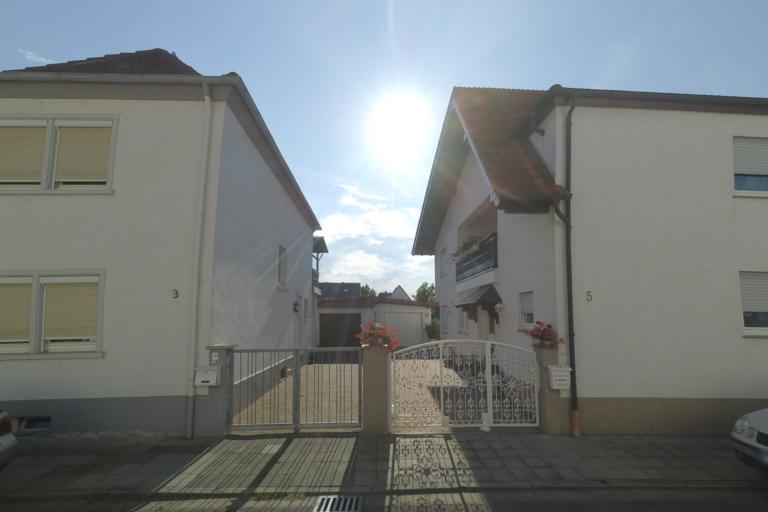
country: DE
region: Rheinland-Pfalz
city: Frankenthal
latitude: 49.5080
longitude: 8.3614
